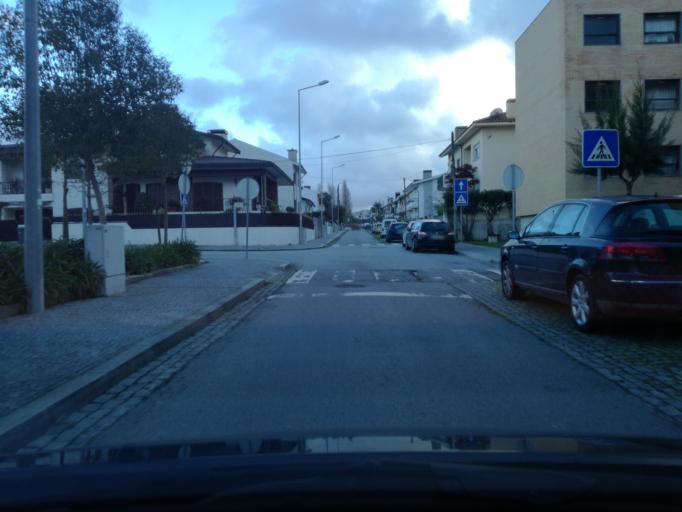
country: PT
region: Porto
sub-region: Maia
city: Gemunde
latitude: 41.2524
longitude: -8.6634
